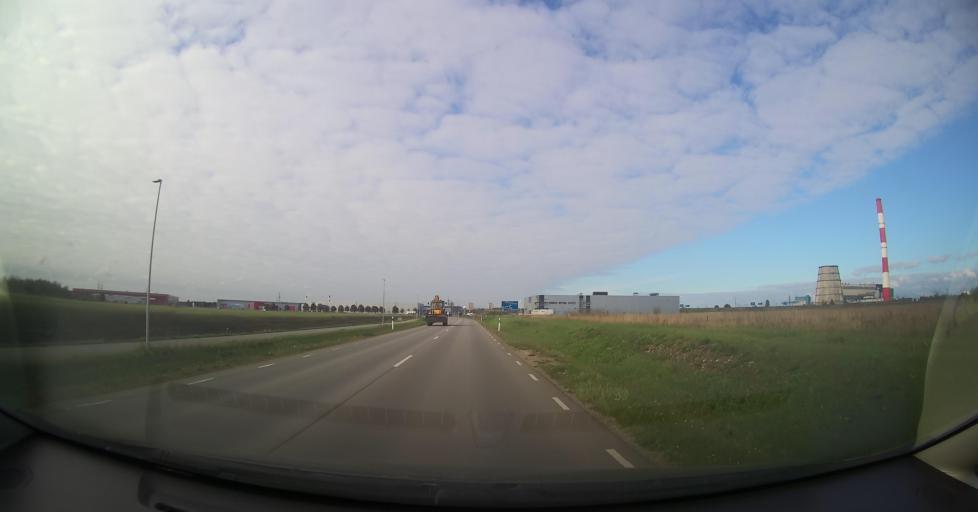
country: EE
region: Harju
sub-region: Joelaehtme vald
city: Loo
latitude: 59.4459
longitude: 24.9383
